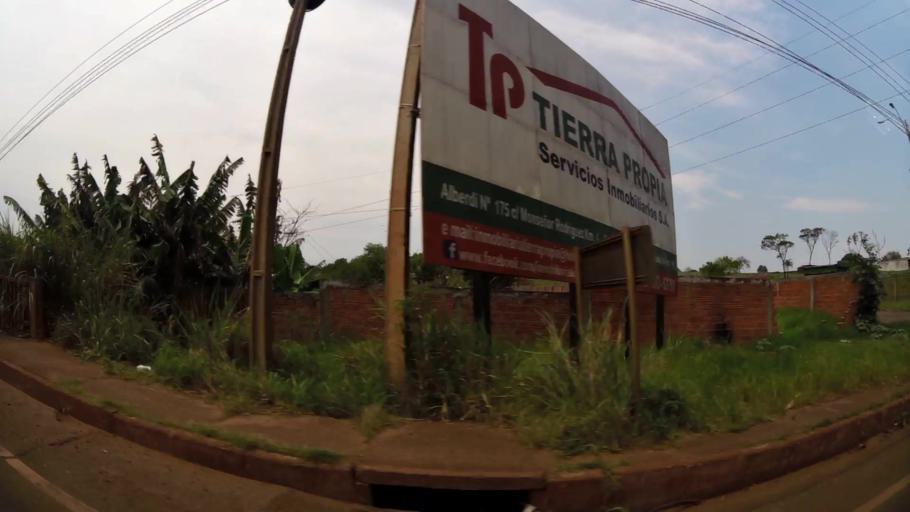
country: PY
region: Alto Parana
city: Ciudad del Este
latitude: -25.4924
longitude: -54.6320
